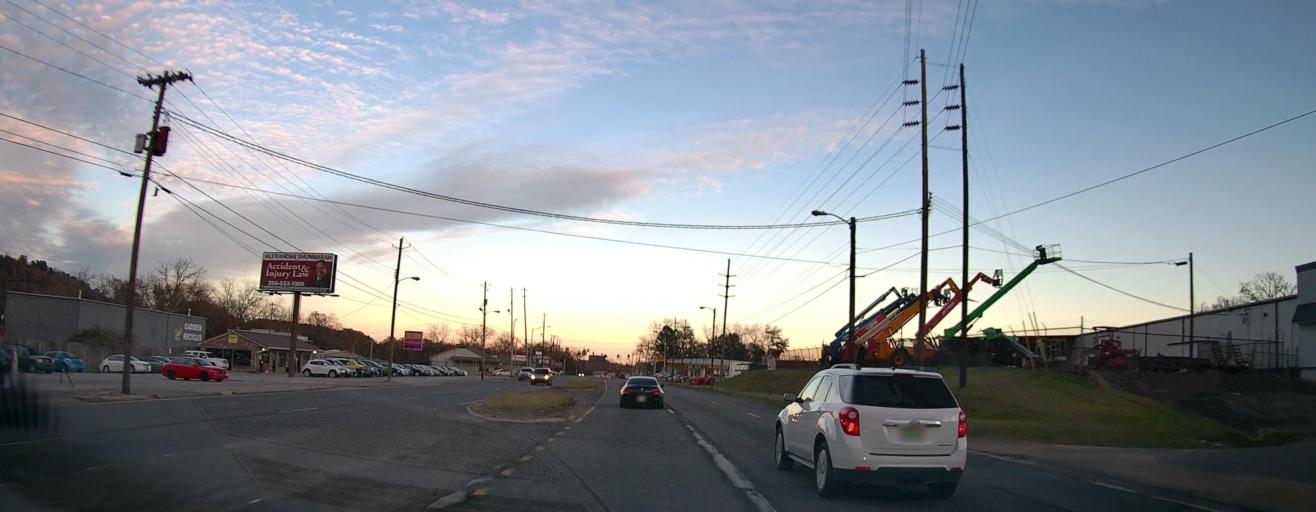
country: US
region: Alabama
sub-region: Etowah County
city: Gadsden
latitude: 34.0177
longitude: -86.0101
